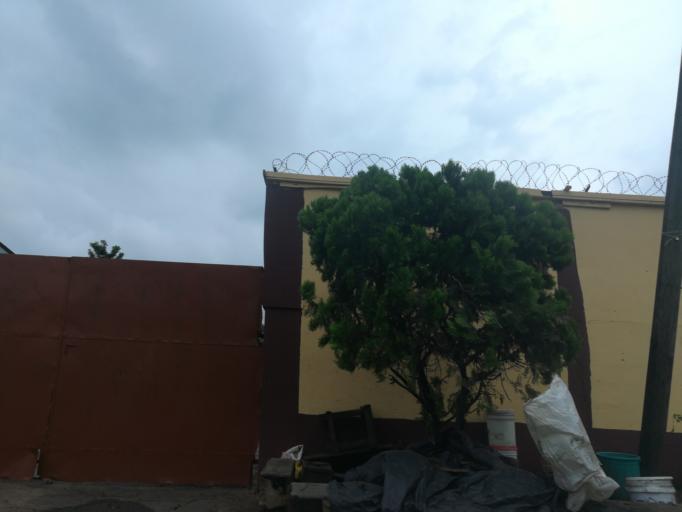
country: NG
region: Lagos
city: Ojota
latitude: 6.5724
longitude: 3.3696
